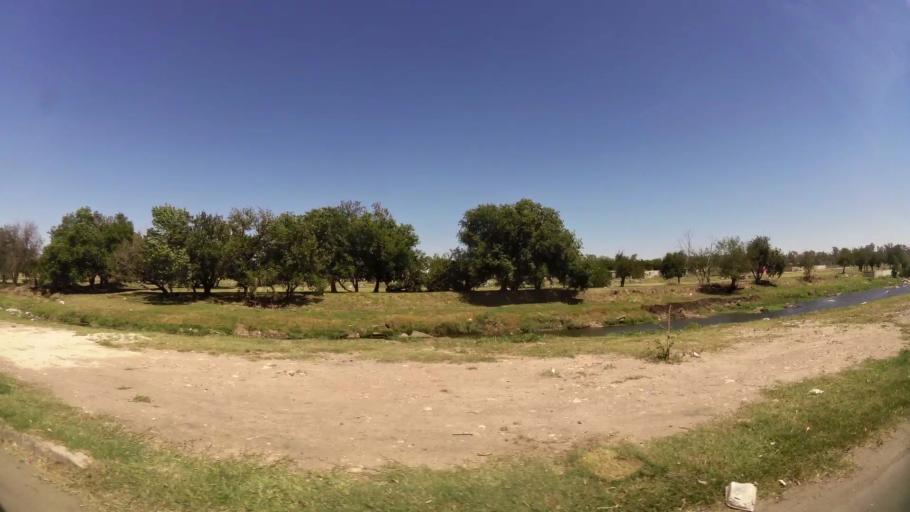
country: AR
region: Cordoba
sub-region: Departamento de Capital
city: Cordoba
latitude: -31.4134
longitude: -64.1415
